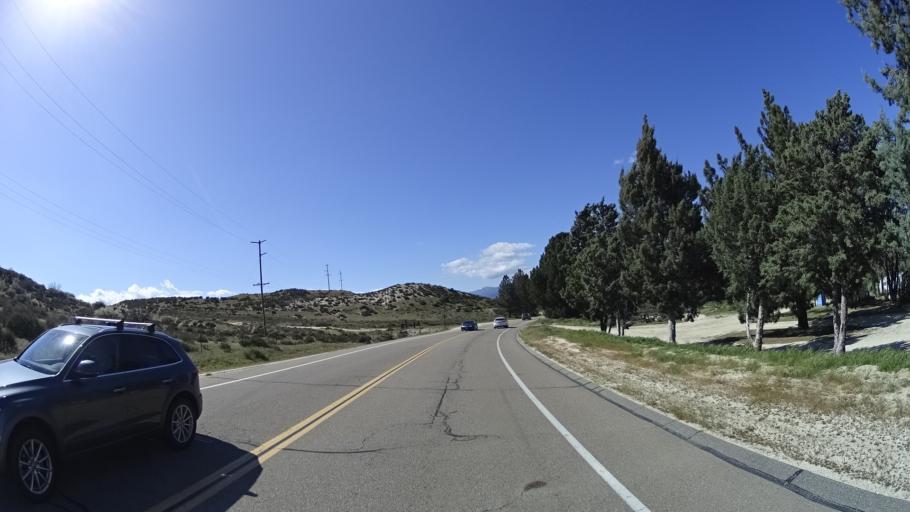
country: US
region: California
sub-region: San Diego County
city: Julian
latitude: 33.2422
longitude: -116.6663
